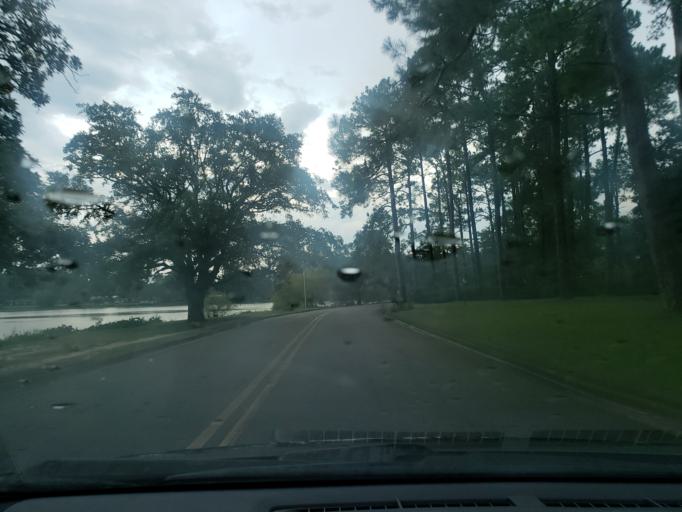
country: US
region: Georgia
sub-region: Dougherty County
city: Albany
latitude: 31.5995
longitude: -84.2032
